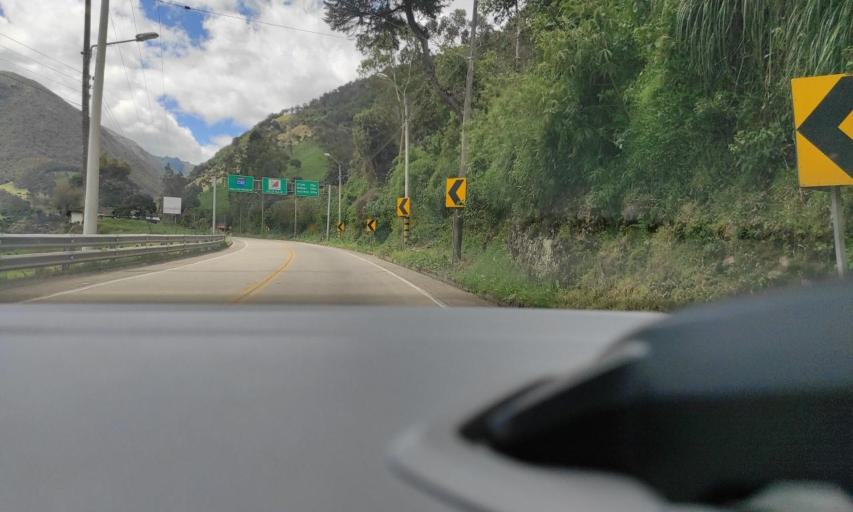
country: EC
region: Azuay
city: Cuenca
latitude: -2.8453
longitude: -79.1166
